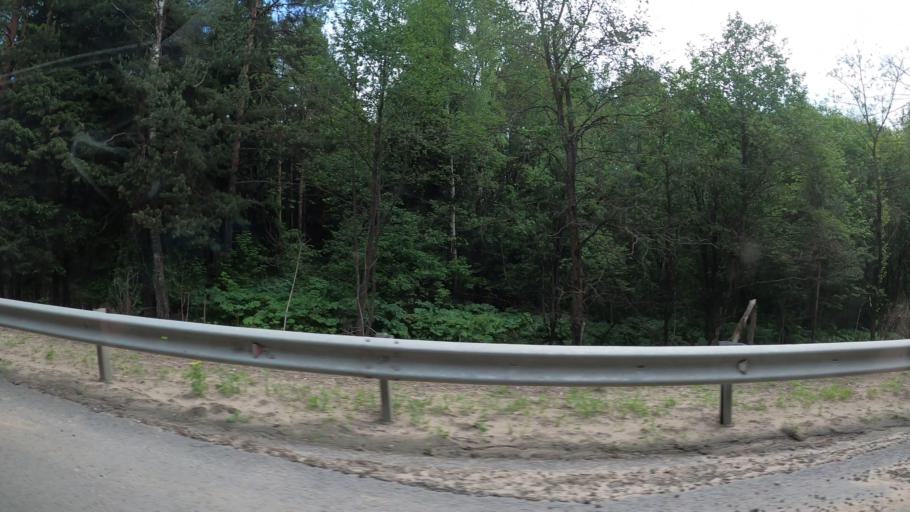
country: RU
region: Moskovskaya
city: Krasnoarmeysk
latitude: 56.0295
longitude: 38.1838
